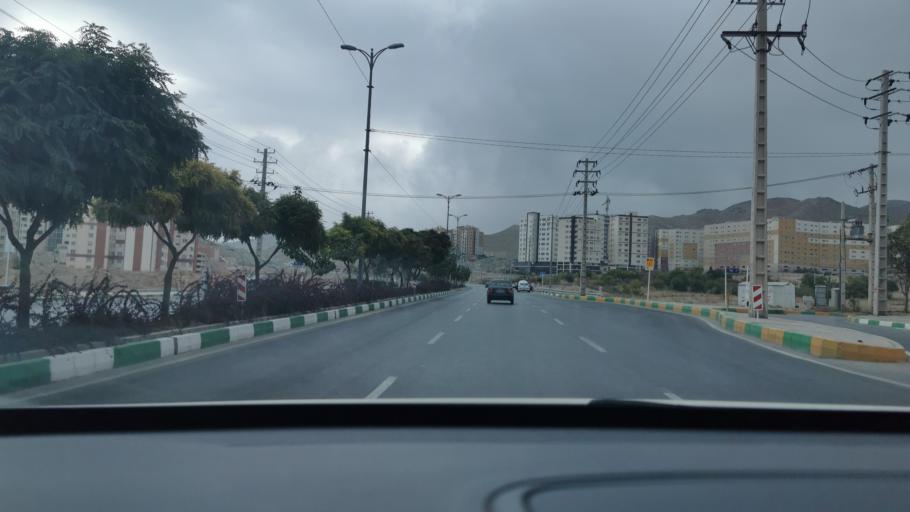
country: IR
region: Razavi Khorasan
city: Mashhad
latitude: 36.2714
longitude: 59.5389
